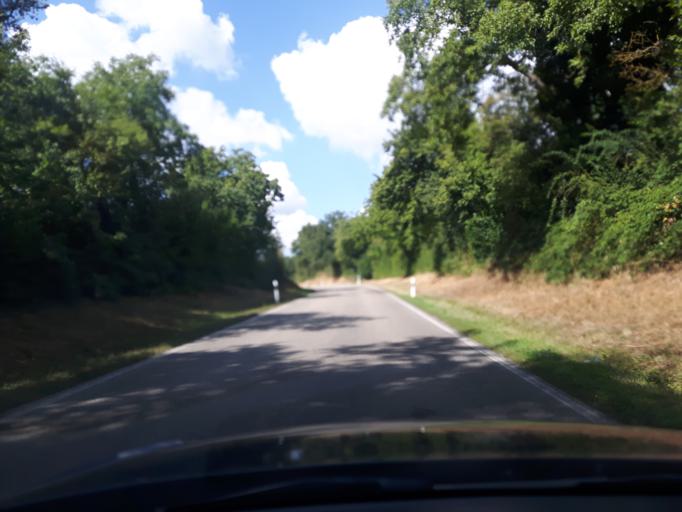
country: DE
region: Baden-Wuerttemberg
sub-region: Karlsruhe Region
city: Sinsheim
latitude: 49.2093
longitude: 8.8730
